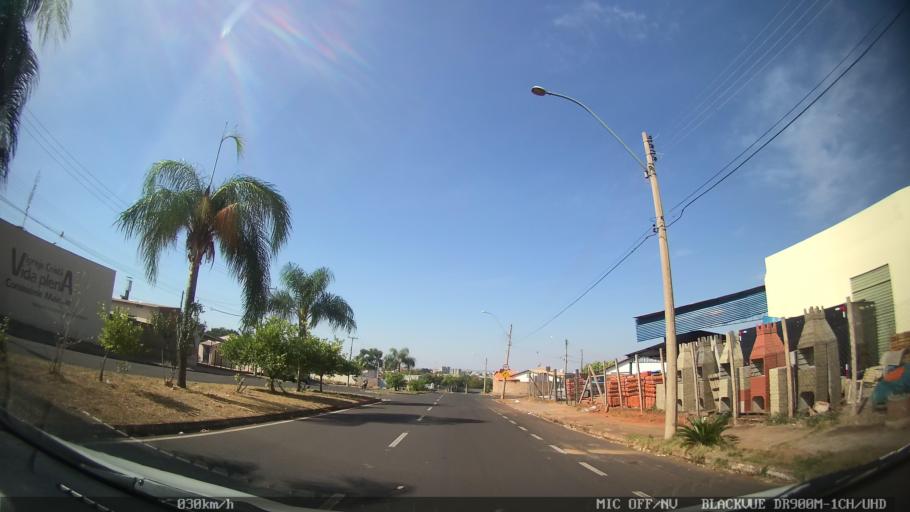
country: BR
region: Sao Paulo
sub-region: Sao Jose Do Rio Preto
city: Sao Jose do Rio Preto
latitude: -20.7905
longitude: -49.4369
